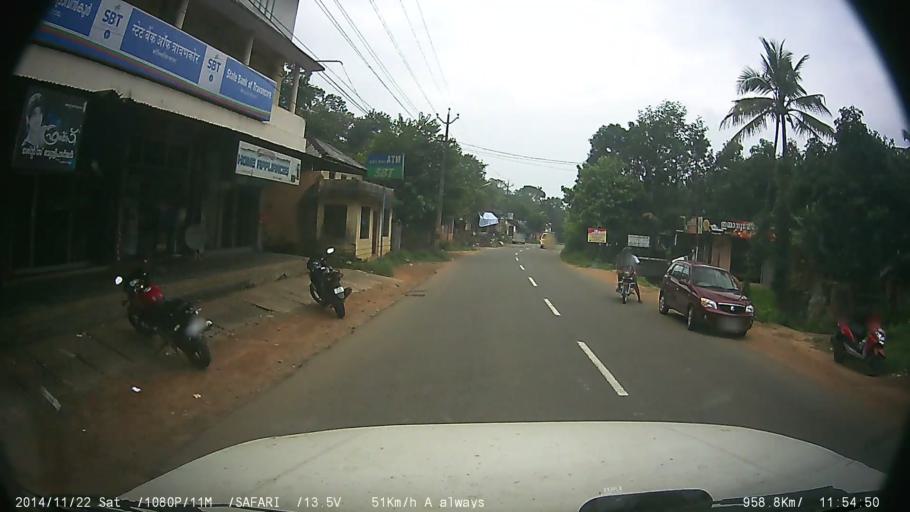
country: IN
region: Kerala
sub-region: Kottayam
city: Palackattumala
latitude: 9.8072
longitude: 76.5753
